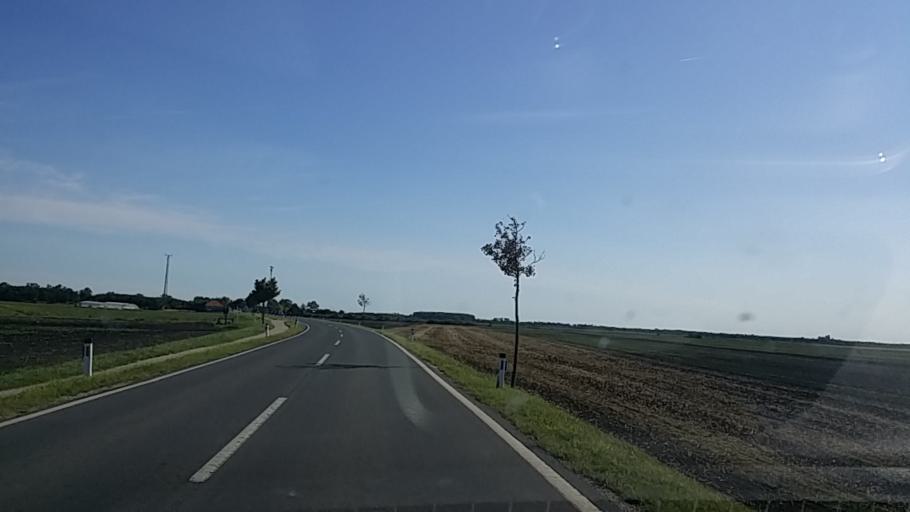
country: AT
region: Burgenland
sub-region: Politischer Bezirk Neusiedl am See
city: Pamhagen
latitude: 47.6931
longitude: 16.9110
